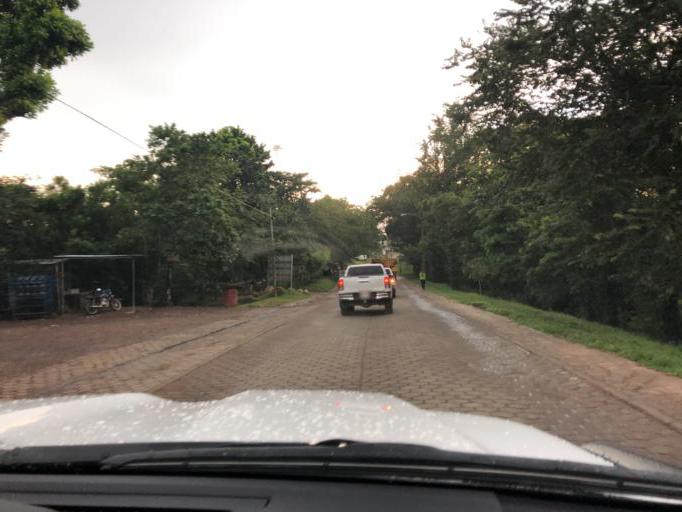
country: NI
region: Chontales
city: La Libertad
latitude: 12.2131
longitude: -85.1710
